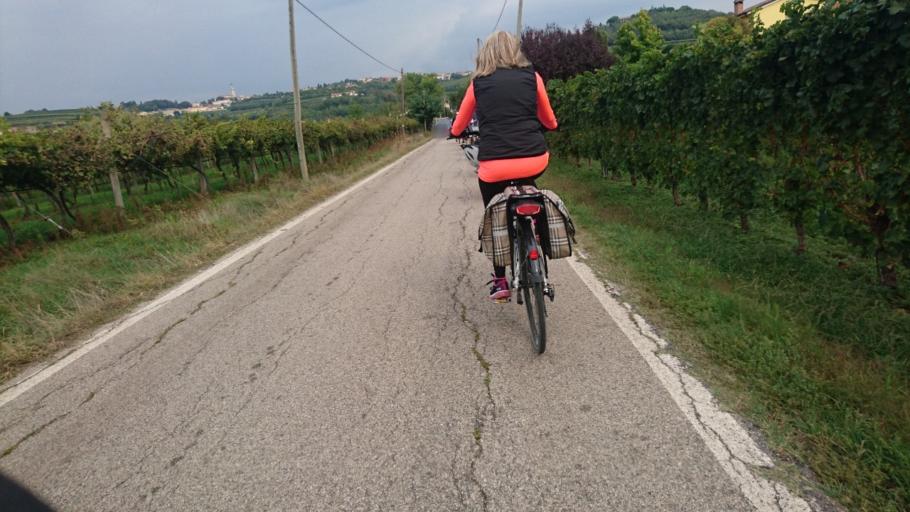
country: IT
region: Veneto
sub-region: Provincia di Verona
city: Caldiero
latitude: 45.4175
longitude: 11.1964
